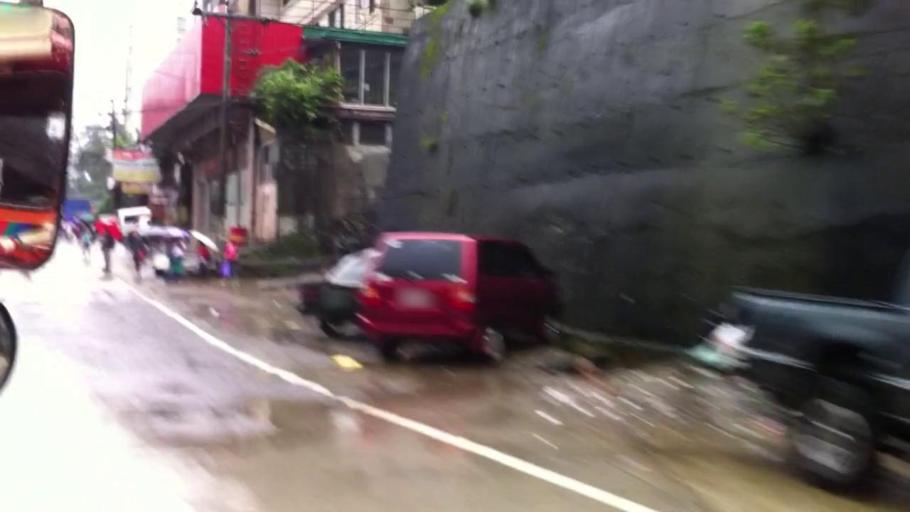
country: PH
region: Cordillera
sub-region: Baguio City
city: Baguio
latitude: 16.4304
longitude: 120.5965
